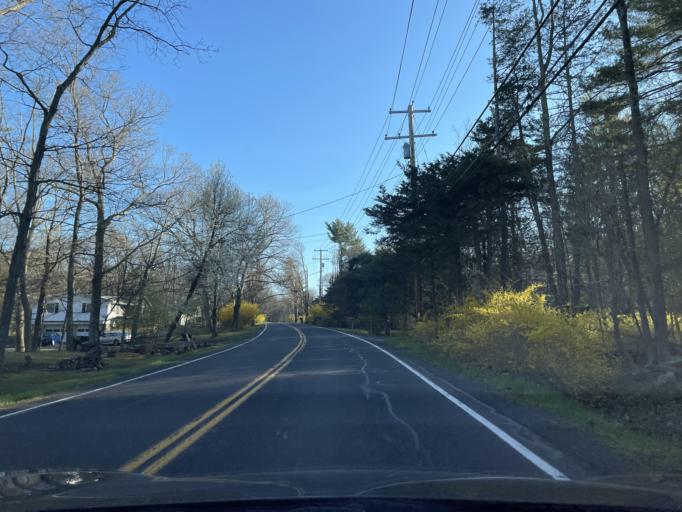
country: US
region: New York
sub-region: Ulster County
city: Woodstock
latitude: 42.0210
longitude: -74.1105
